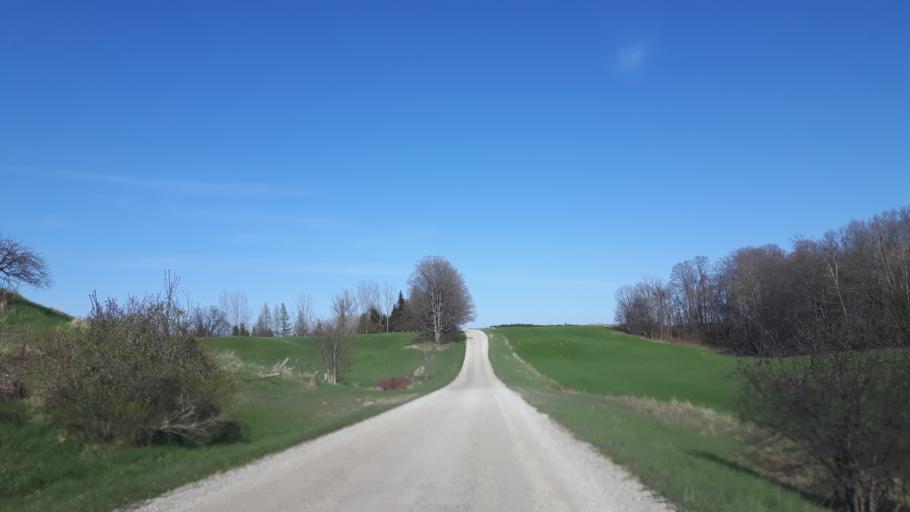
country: CA
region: Ontario
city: Goderich
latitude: 43.6613
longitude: -81.6778
